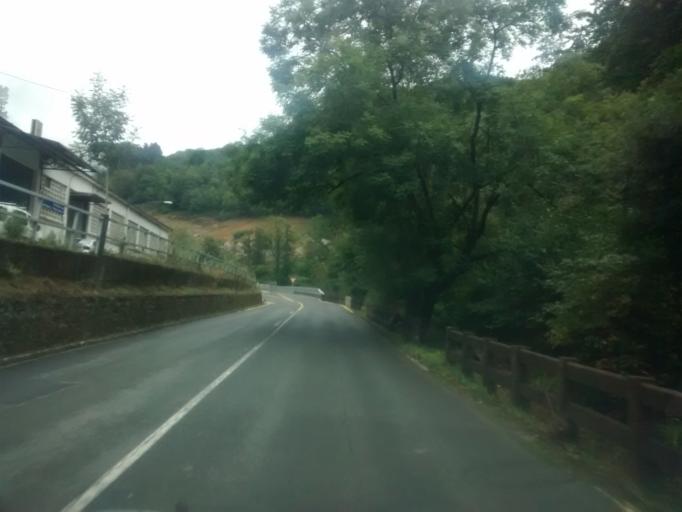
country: ES
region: Basque Country
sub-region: Provincia de Guipuzcoa
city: Bergara
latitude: 43.1088
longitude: -2.4082
